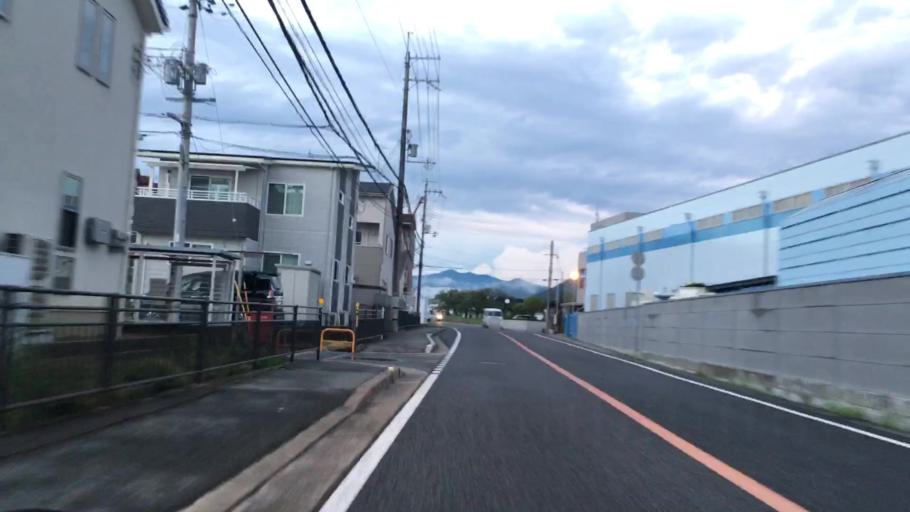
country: JP
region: Hyogo
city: Himeji
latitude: 34.9456
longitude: 134.7471
